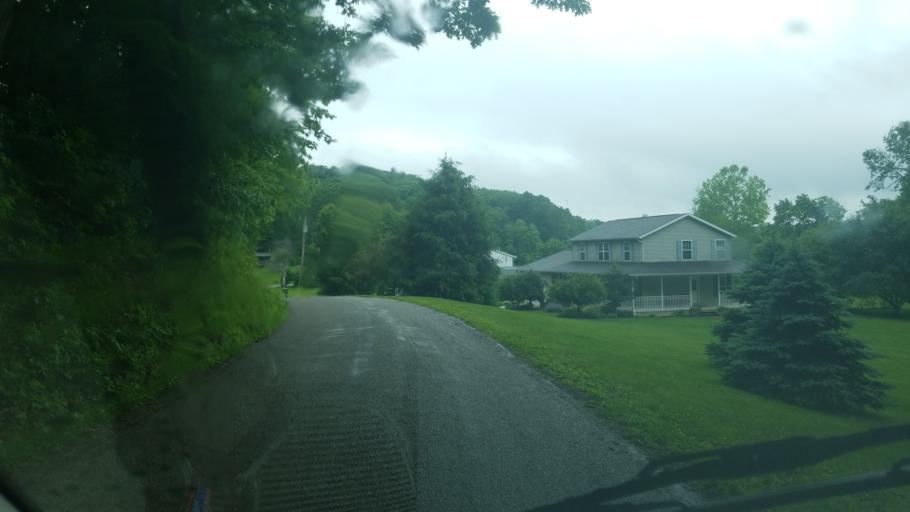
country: US
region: Ohio
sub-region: Sandusky County
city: Bellville
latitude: 40.6096
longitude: -82.4571
